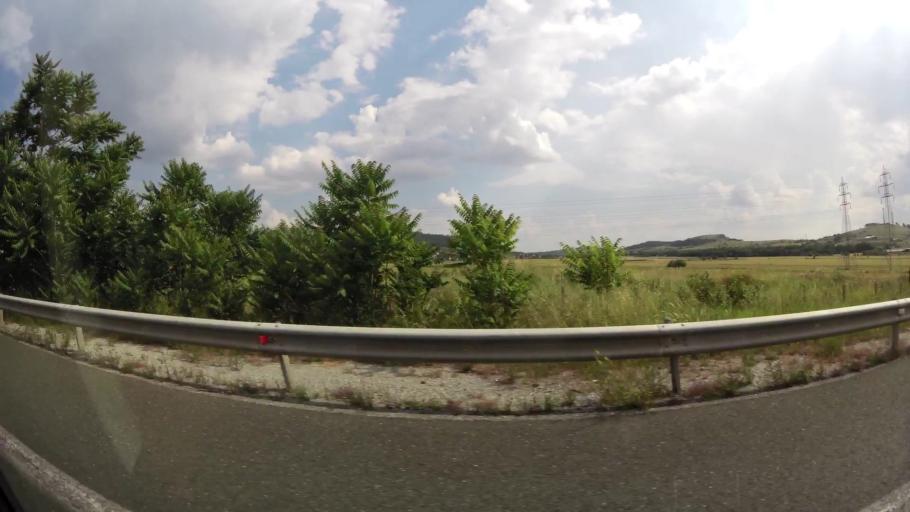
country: GR
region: West Macedonia
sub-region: Nomos Kozanis
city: Koila
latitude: 40.3618
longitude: 21.8305
